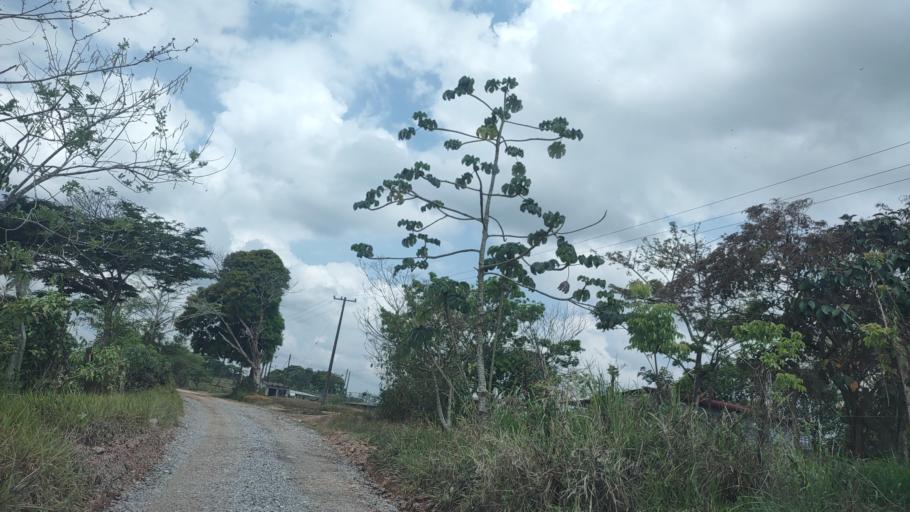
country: MX
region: Veracruz
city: Las Choapas
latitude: 17.9568
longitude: -94.1116
